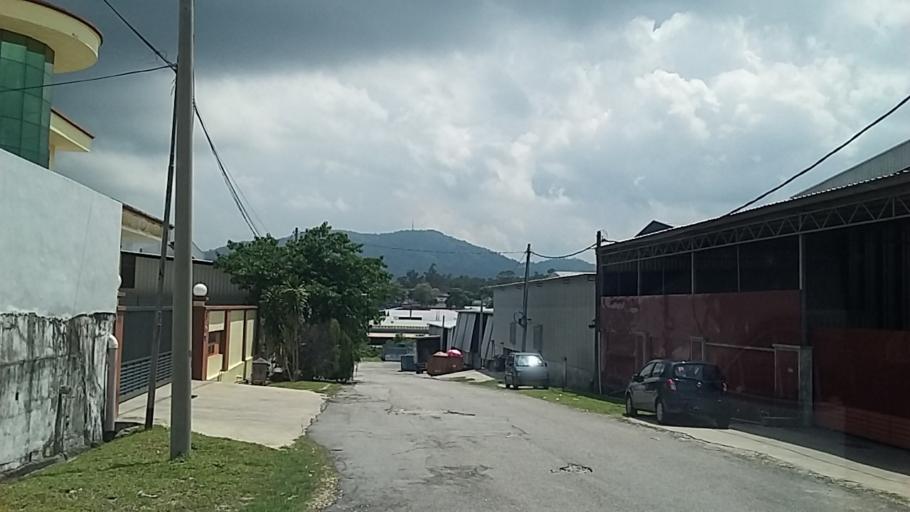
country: MY
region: Johor
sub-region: Daerah Batu Pahat
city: Batu Pahat
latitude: 1.7825
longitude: 102.9658
